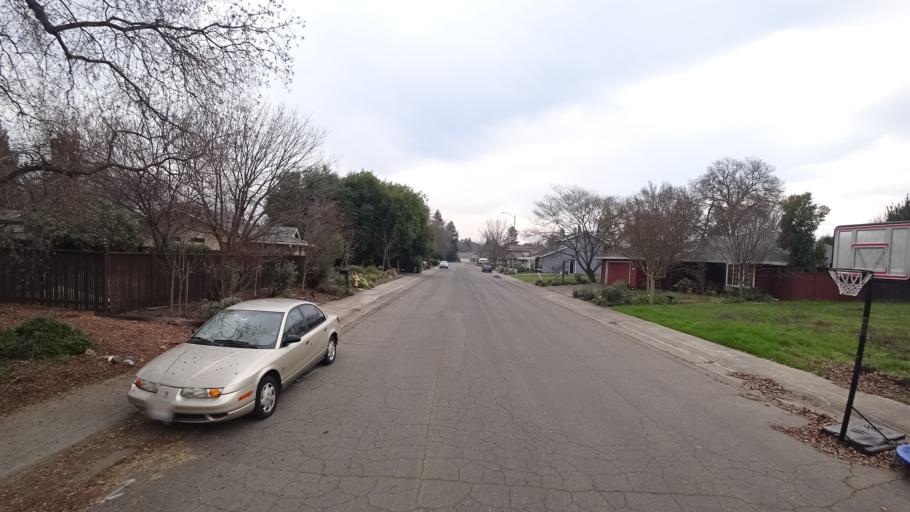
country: US
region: California
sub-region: Yolo County
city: Davis
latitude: 38.5449
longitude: -121.7102
